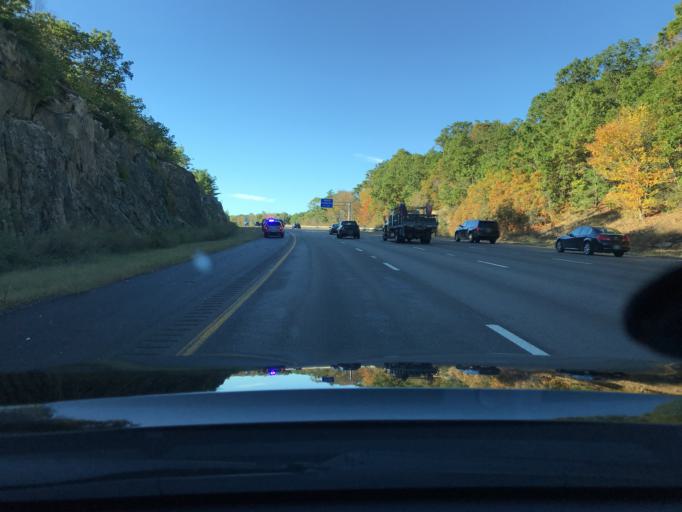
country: US
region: Massachusetts
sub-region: Norfolk County
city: Needham
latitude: 42.2627
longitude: -71.2088
